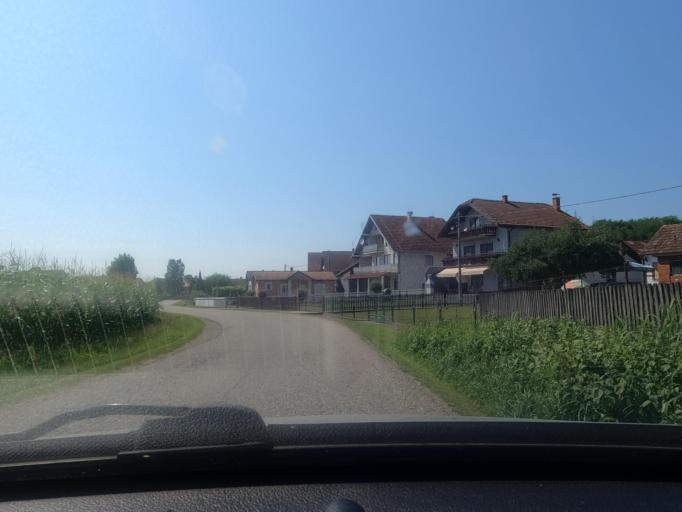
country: RS
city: Jadranska Lesnica
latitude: 44.5452
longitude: 19.3593
